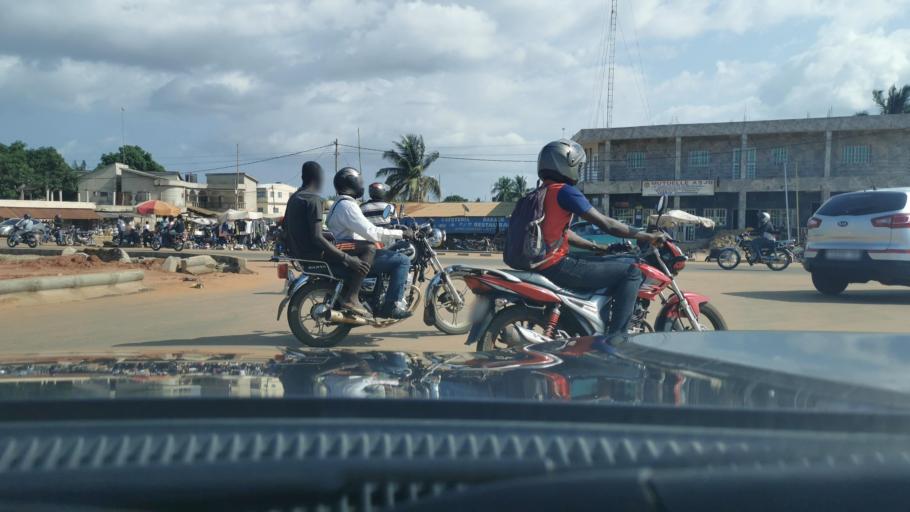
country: TG
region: Maritime
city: Lome
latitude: 6.2076
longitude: 1.1405
